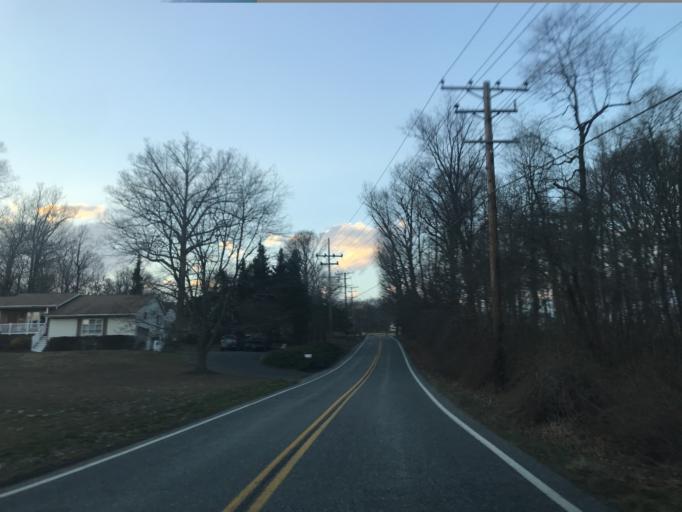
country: US
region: Maryland
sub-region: Harford County
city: Bel Air South
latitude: 39.5271
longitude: -76.2783
